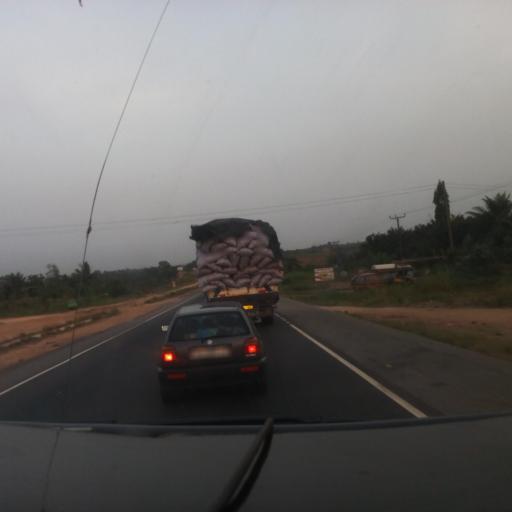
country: GH
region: Eastern
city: Nsawam
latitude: 5.8934
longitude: -0.3838
